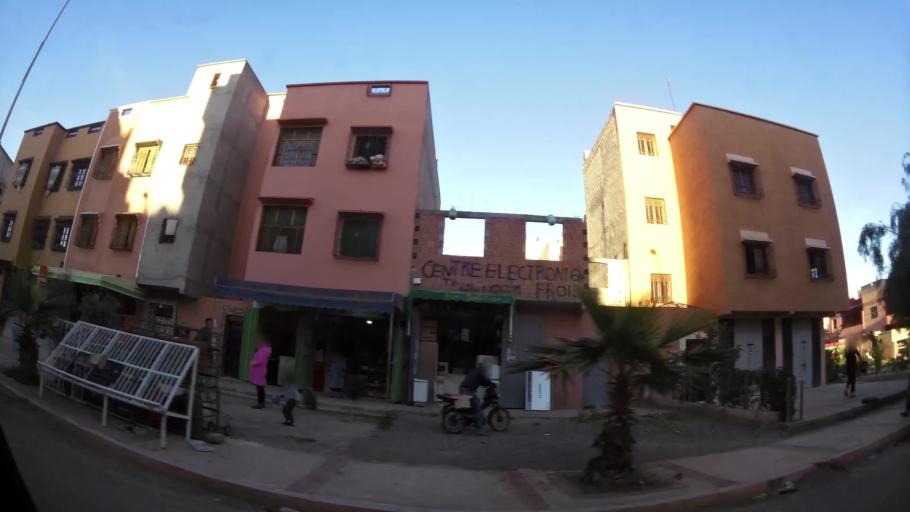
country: MA
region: Marrakech-Tensift-Al Haouz
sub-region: Marrakech
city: Marrakesh
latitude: 31.7436
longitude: -8.1099
